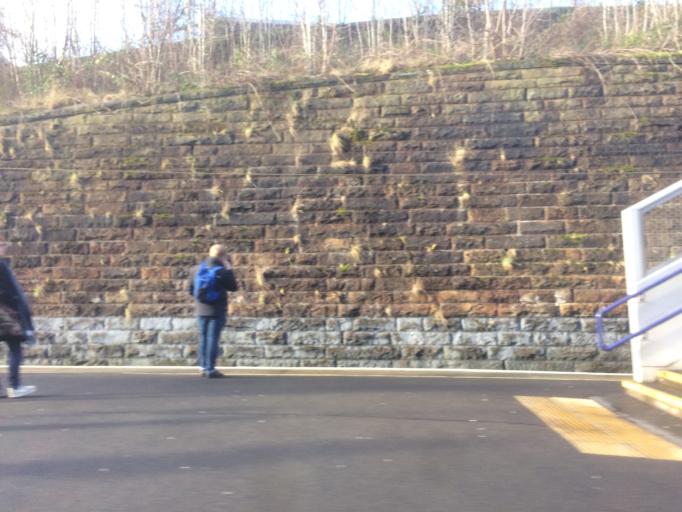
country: GB
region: Scotland
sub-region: Glasgow City
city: Glasgow
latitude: 55.8272
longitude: -4.2609
